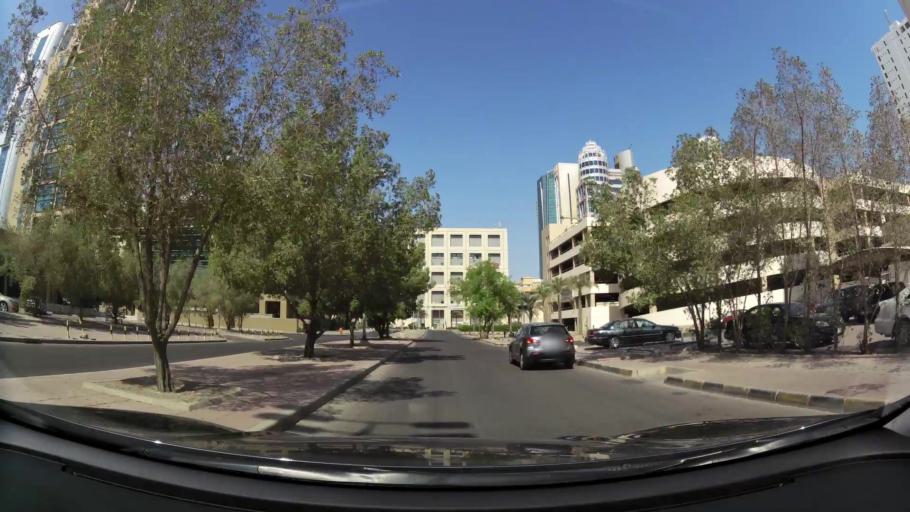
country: KW
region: Al Asimah
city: Kuwait City
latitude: 29.3812
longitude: 47.9882
